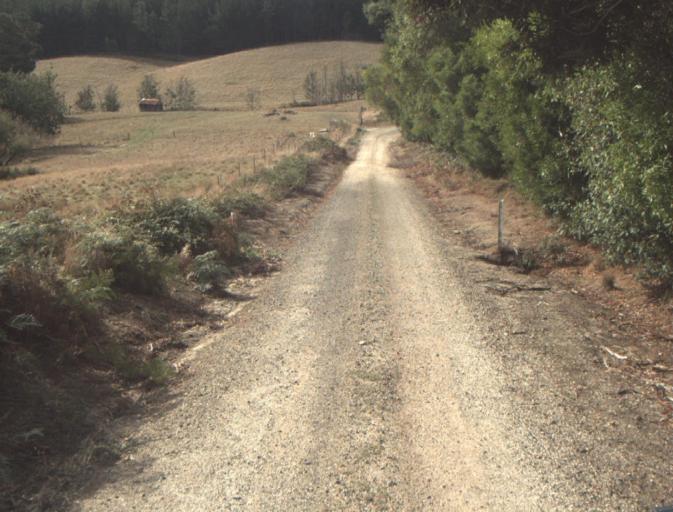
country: AU
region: Tasmania
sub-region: Launceston
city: Mayfield
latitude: -41.1820
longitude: 147.1941
